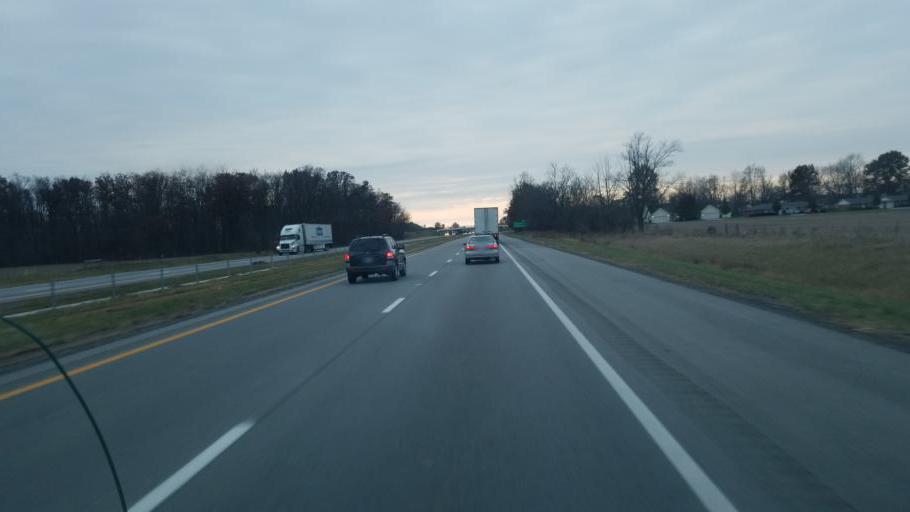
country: US
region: Ohio
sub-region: Auglaize County
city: Cridersville
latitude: 40.6611
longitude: -84.1316
